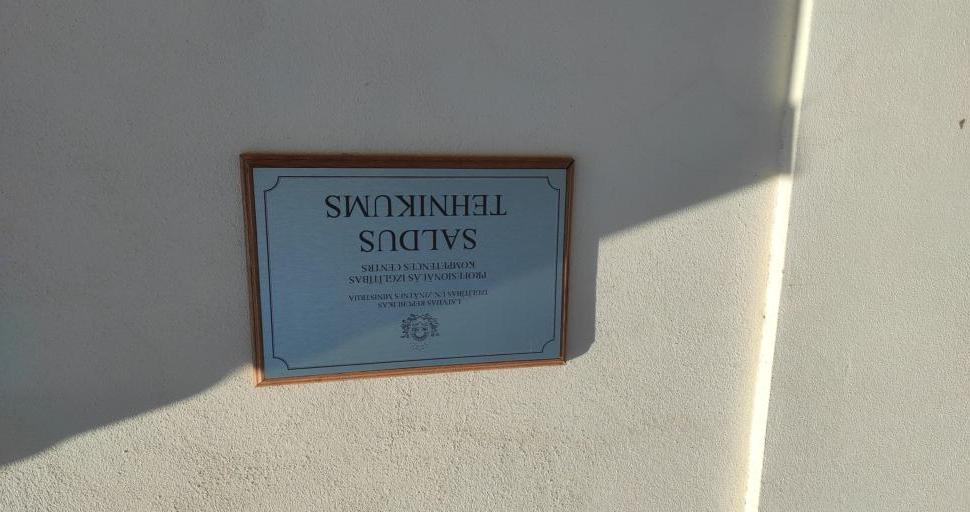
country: LV
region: Saldus Rajons
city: Saldus
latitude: 56.6668
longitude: 22.5146
